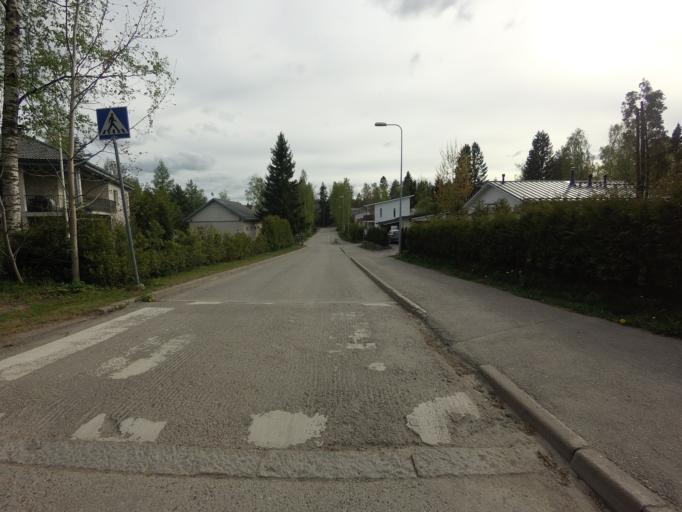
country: FI
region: Uusimaa
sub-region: Helsinki
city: Kauniainen
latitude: 60.1961
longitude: 24.7166
